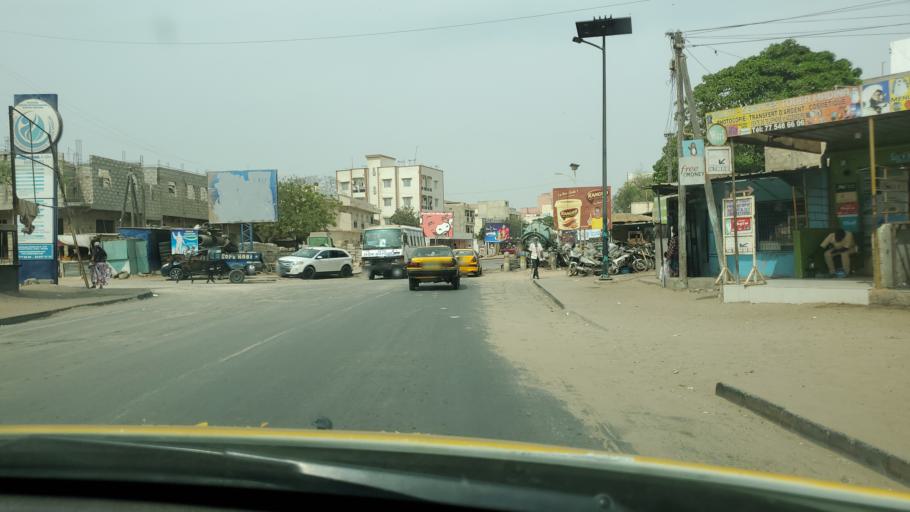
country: SN
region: Dakar
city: Pikine
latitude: 14.7699
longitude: -17.3942
